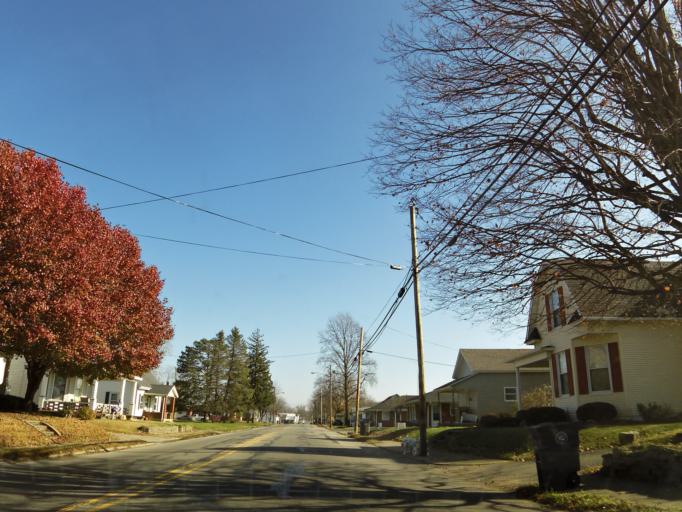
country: US
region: Indiana
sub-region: Fayette County
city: Connersville
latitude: 39.6391
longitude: -85.1233
